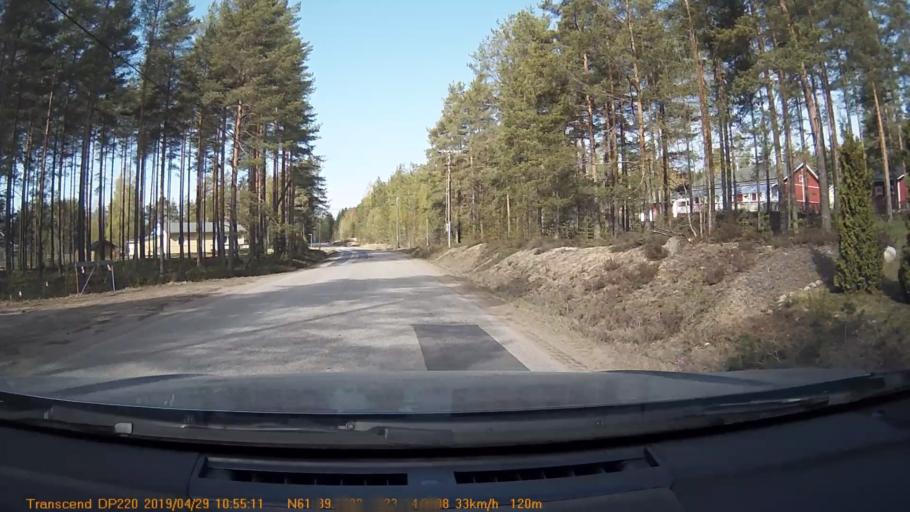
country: FI
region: Pirkanmaa
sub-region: Tampere
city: Haemeenkyroe
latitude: 61.6628
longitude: 23.2347
